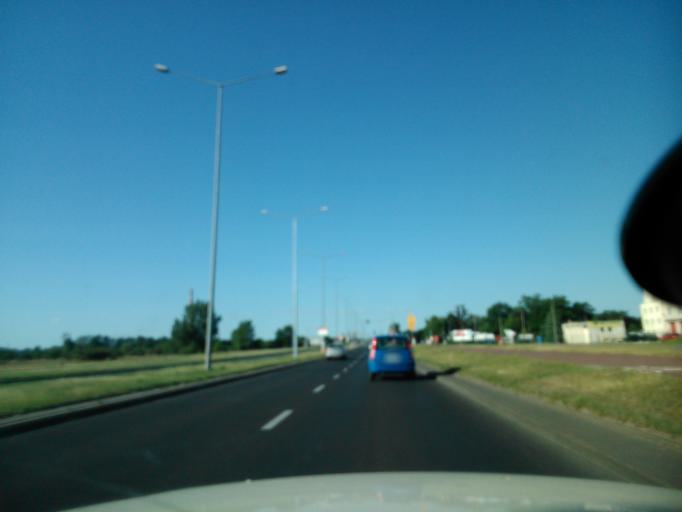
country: PL
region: Kujawsko-Pomorskie
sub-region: Powiat torunski
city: Lubicz Dolny
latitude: 53.0305
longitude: 18.6870
